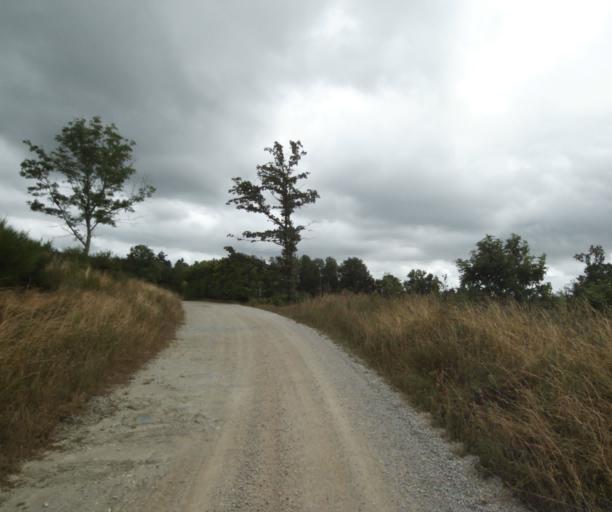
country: FR
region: Midi-Pyrenees
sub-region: Departement du Tarn
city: Soreze
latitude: 43.4243
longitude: 2.1212
